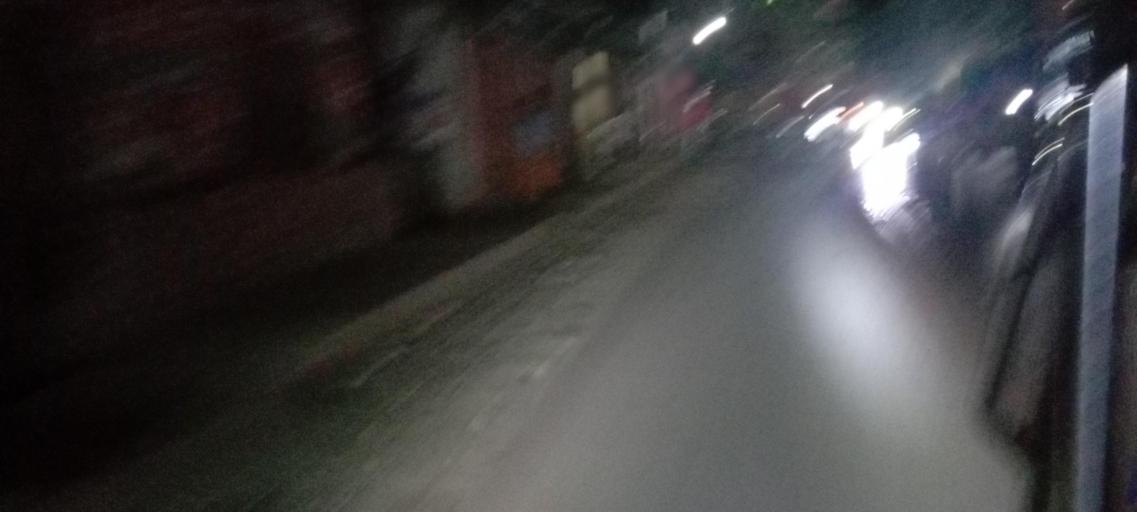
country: BD
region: Dhaka
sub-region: Dhaka
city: Dhaka
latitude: 23.7006
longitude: 90.3853
